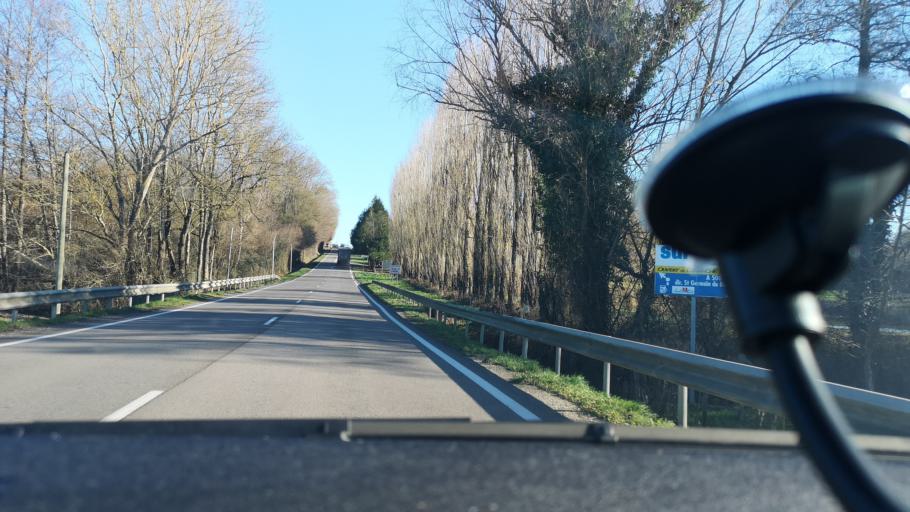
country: FR
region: Bourgogne
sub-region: Departement de Saone-et-Loire
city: Mervans
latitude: 46.7432
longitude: 5.1157
